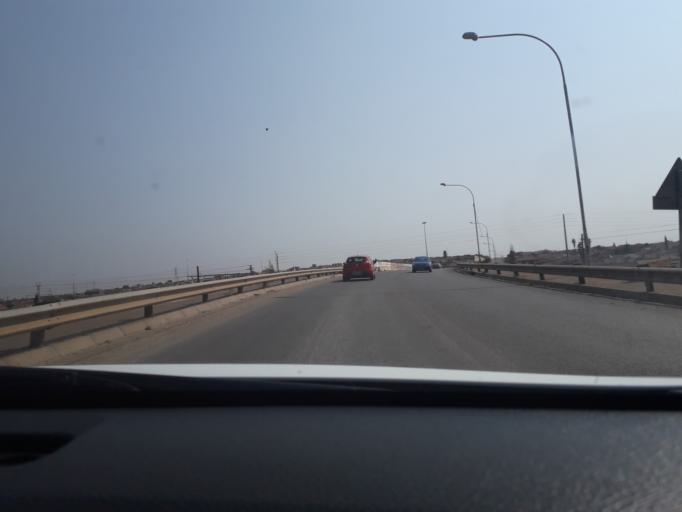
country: ZA
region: Gauteng
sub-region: Ekurhuleni Metropolitan Municipality
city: Tembisa
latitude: -25.9901
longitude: 28.2475
